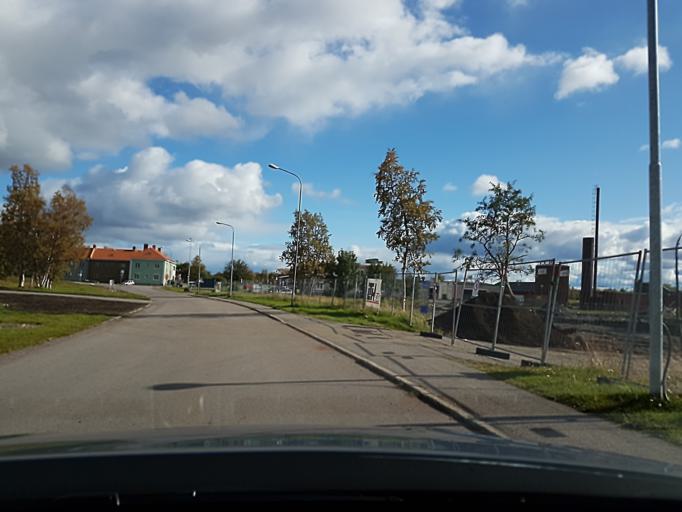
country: SE
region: Norrbotten
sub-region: Kiruna Kommun
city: Kiruna
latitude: 67.8461
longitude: 20.2277
